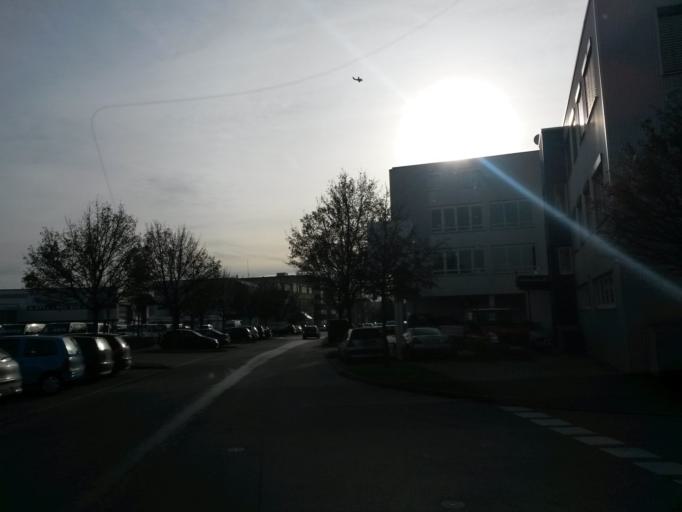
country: DE
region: Baden-Wuerttemberg
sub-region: Regierungsbezirk Stuttgart
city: Denkendorf
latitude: 48.7129
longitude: 9.3085
